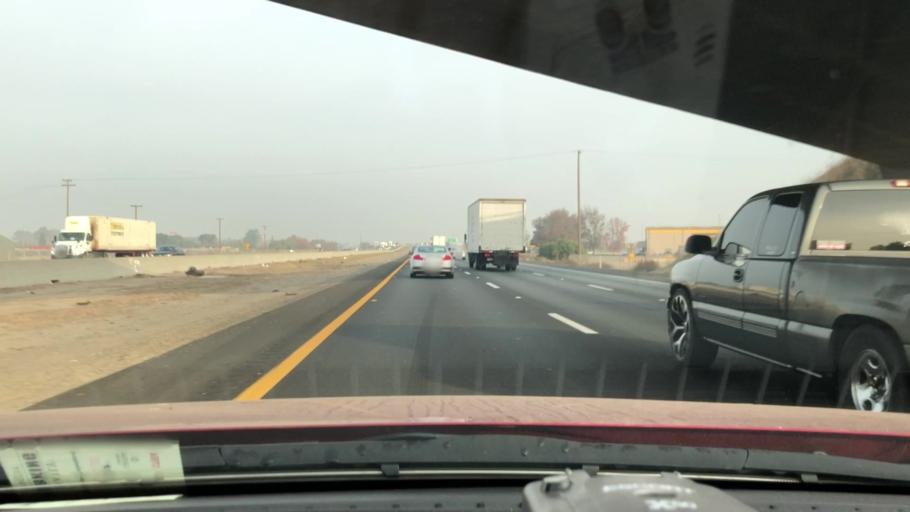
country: US
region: California
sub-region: San Joaquin County
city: French Camp
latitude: 37.8750
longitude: -121.2778
